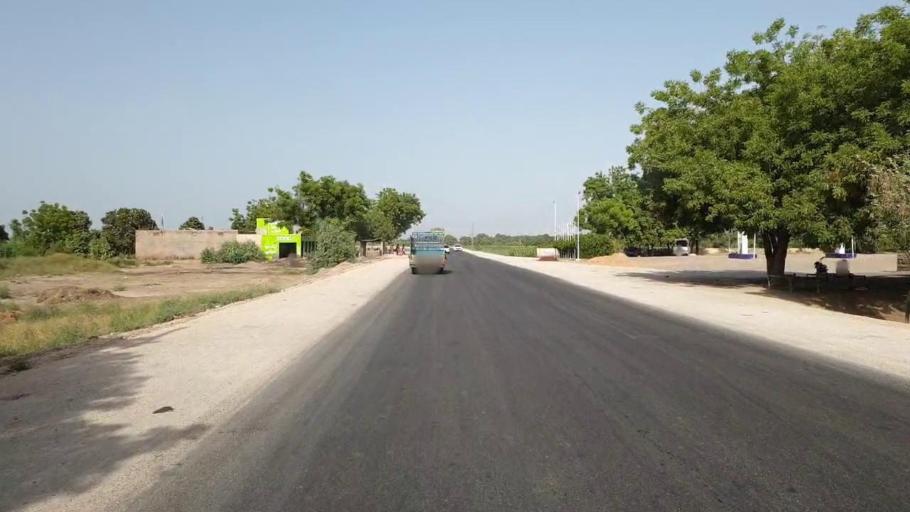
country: PK
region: Sindh
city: Sakrand
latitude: 26.2446
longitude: 68.2849
